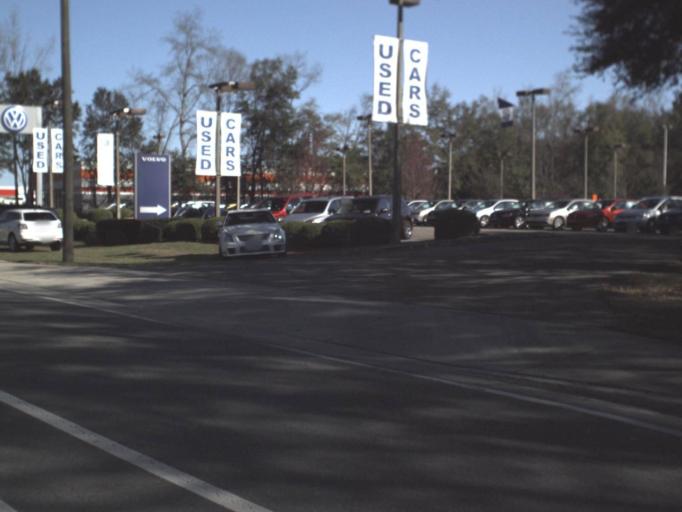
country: US
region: Florida
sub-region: Leon County
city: Tallahassee
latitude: 30.4592
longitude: -84.3584
